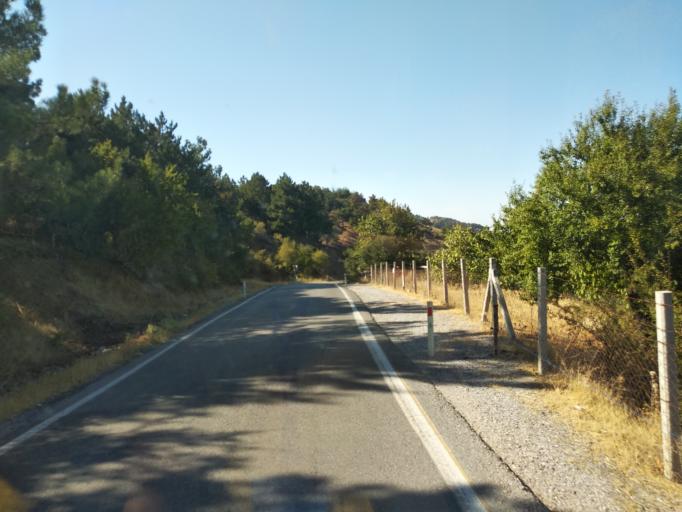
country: TR
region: Izmir
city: Gaziemir
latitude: 38.3205
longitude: 27.0086
